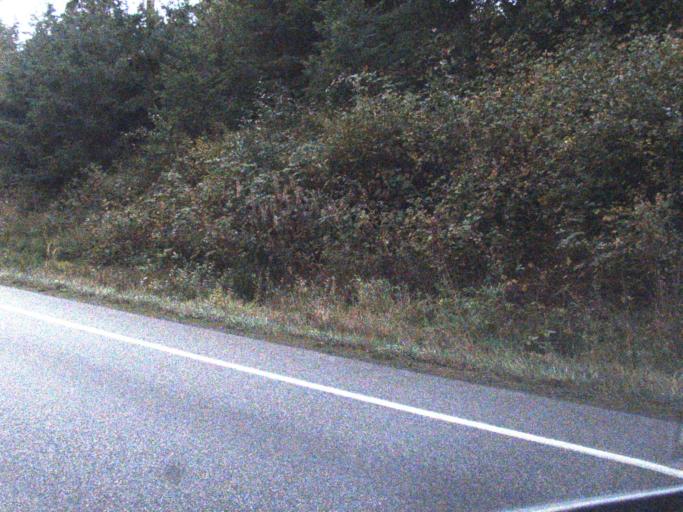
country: US
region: Washington
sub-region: Island County
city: Oak Harbor
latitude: 48.3462
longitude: -122.6141
